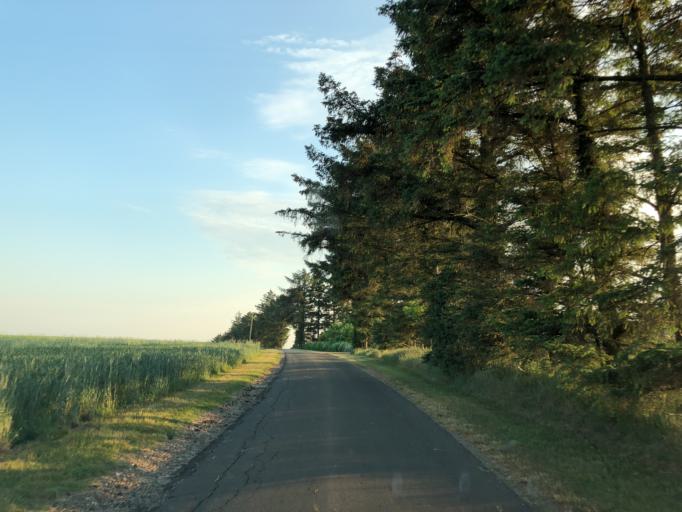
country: DK
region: Central Jutland
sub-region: Holstebro Kommune
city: Holstebro
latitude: 56.3901
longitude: 8.4741
